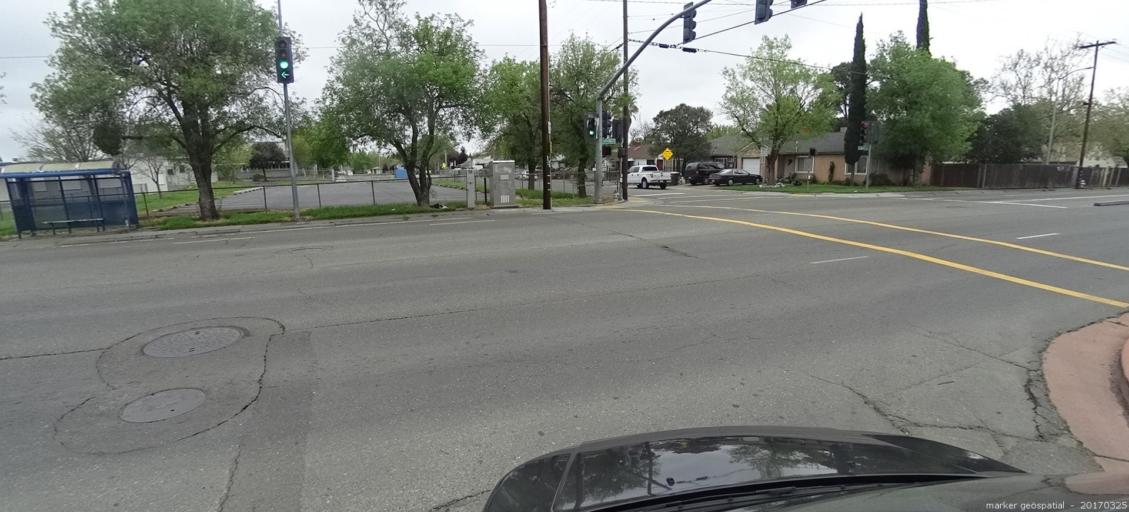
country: US
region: California
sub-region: Sacramento County
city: Florin
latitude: 38.5250
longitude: -121.4171
